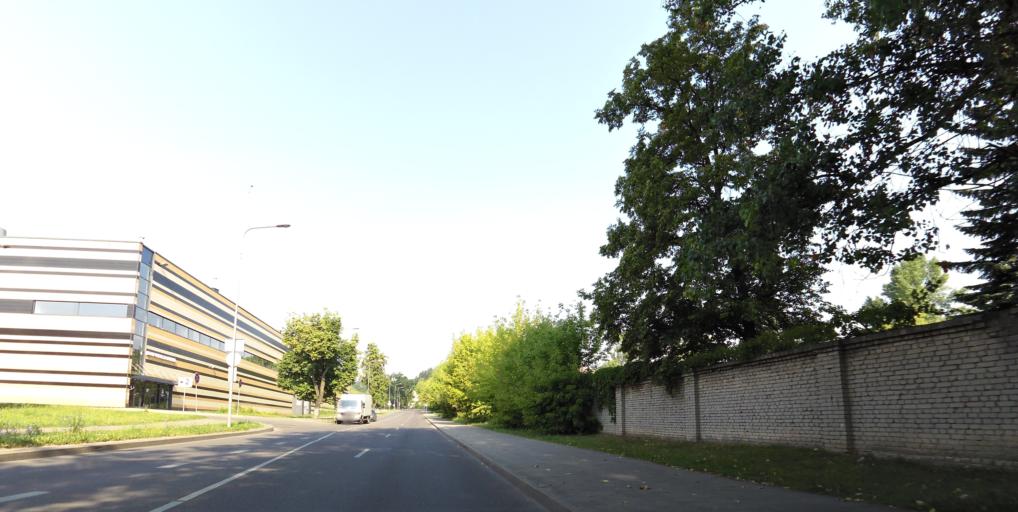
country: LT
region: Vilnius County
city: Seskine
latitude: 54.7007
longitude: 25.2598
